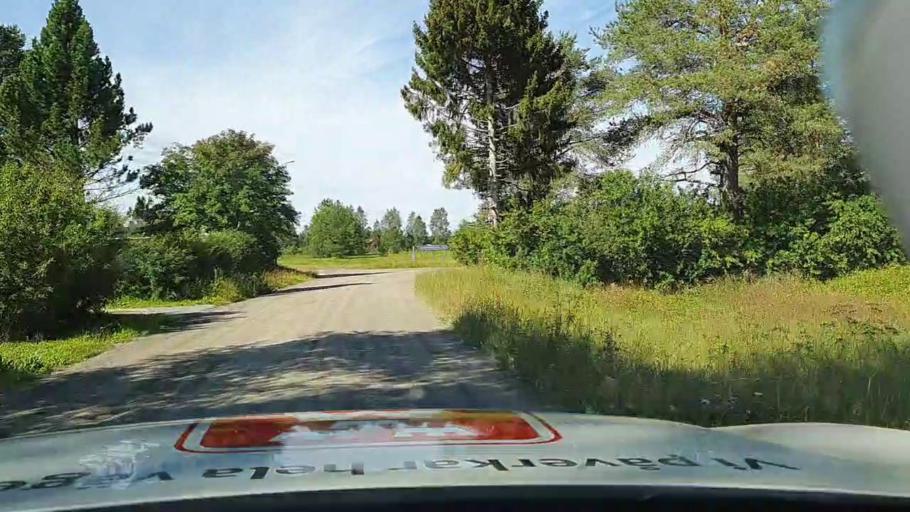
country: SE
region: Jaemtland
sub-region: Stroemsunds Kommun
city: Stroemsund
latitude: 63.6923
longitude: 15.3775
